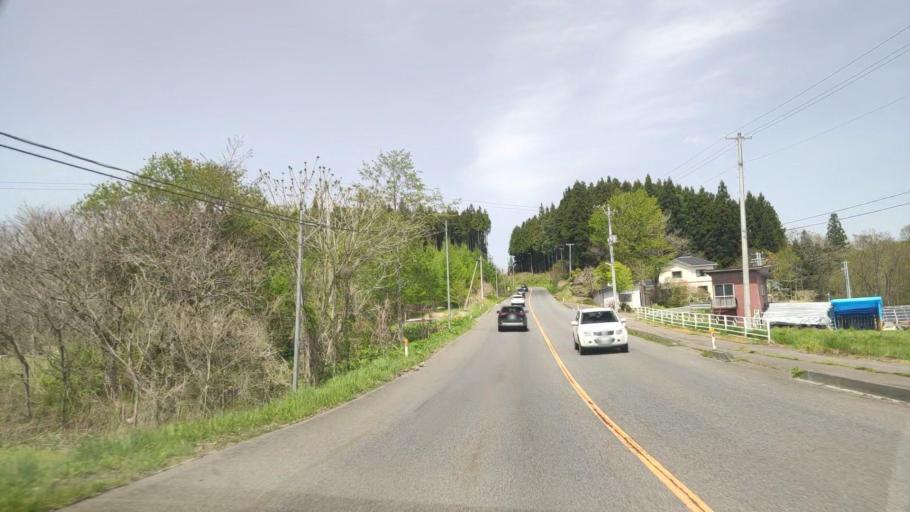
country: JP
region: Aomori
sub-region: Misawa Shi
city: Inuotose
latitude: 40.5636
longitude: 141.3817
